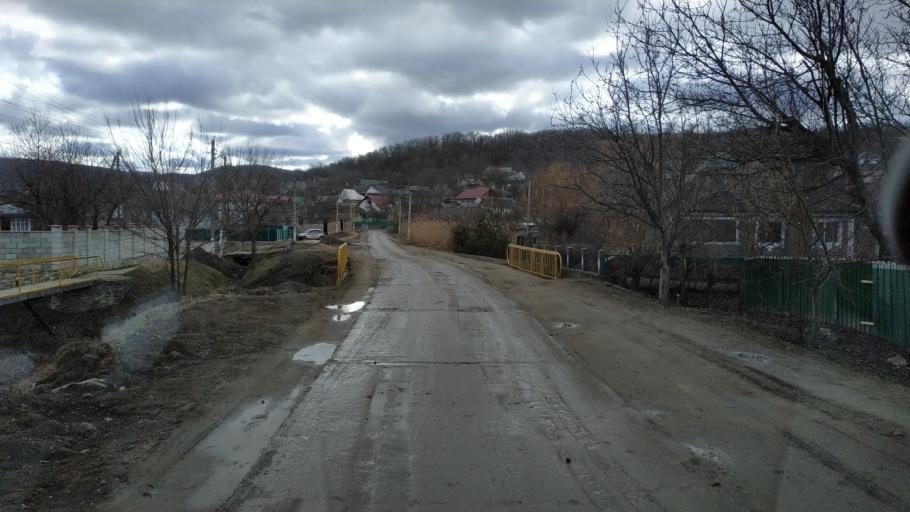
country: MD
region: Stinga Nistrului
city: Bucovat
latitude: 47.1341
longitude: 28.3808
